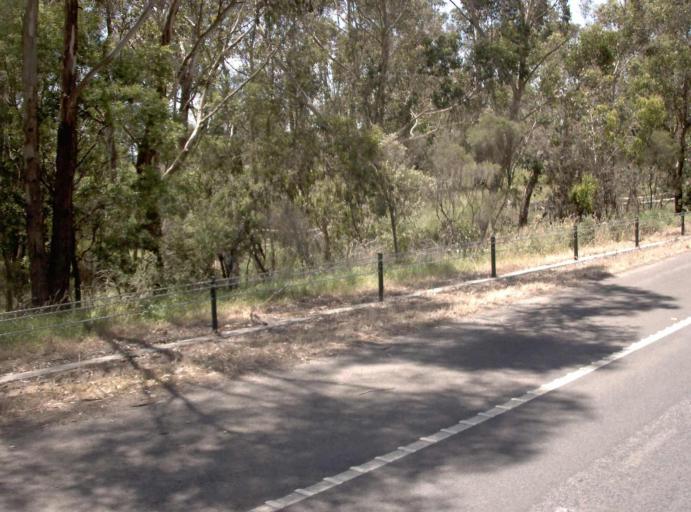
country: AU
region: Victoria
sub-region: Baw Baw
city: Warragul
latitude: -38.0952
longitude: 145.8408
